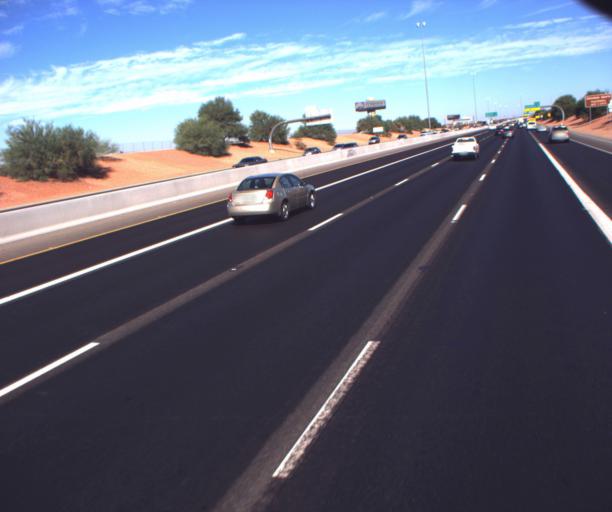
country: US
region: Arizona
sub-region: Maricopa County
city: Tolleson
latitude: 33.4981
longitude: -112.2653
